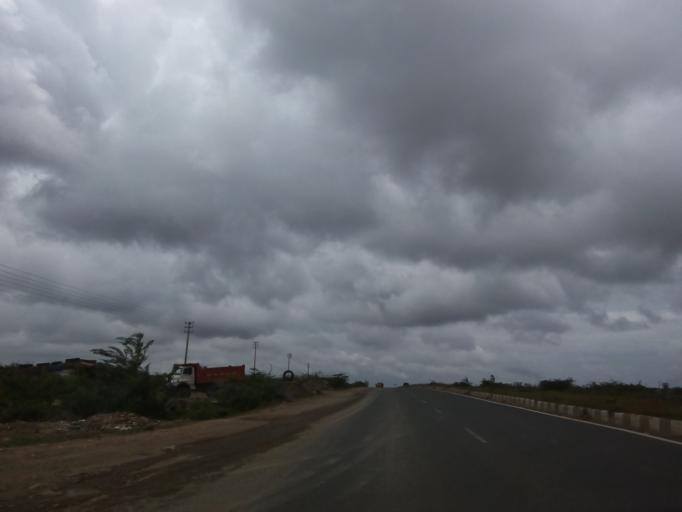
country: IN
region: Karnataka
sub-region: Haveri
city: Ranibennur
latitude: 14.6534
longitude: 75.5692
